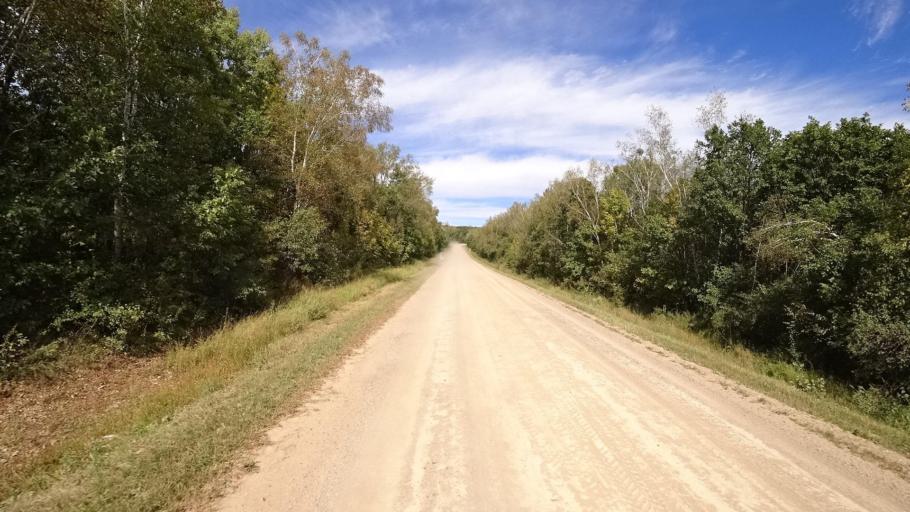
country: RU
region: Primorskiy
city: Yakovlevka
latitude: 44.6552
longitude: 133.5969
